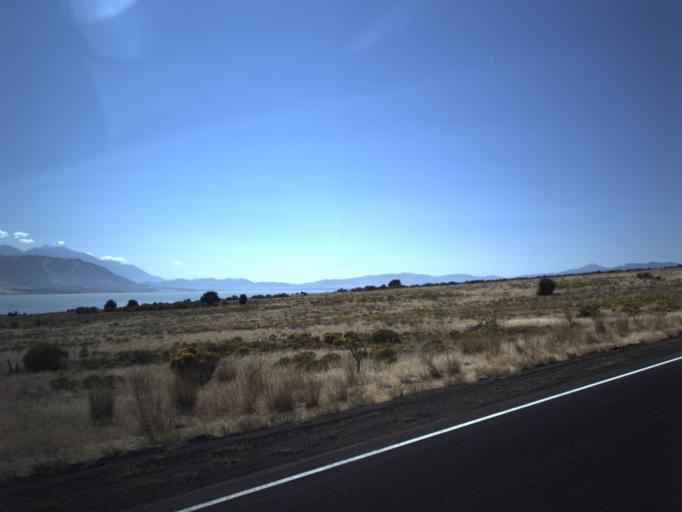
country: US
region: Utah
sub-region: Utah County
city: Saratoga Springs
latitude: 40.2171
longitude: -111.8846
